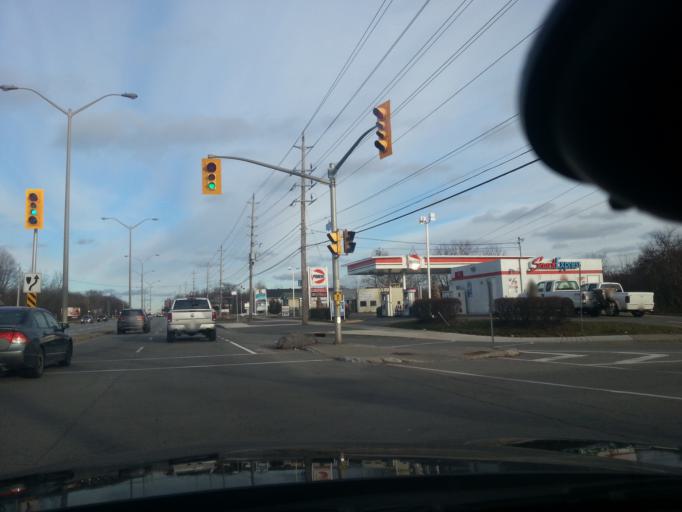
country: CA
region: Ontario
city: Ottawa
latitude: 45.4261
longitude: -75.6317
